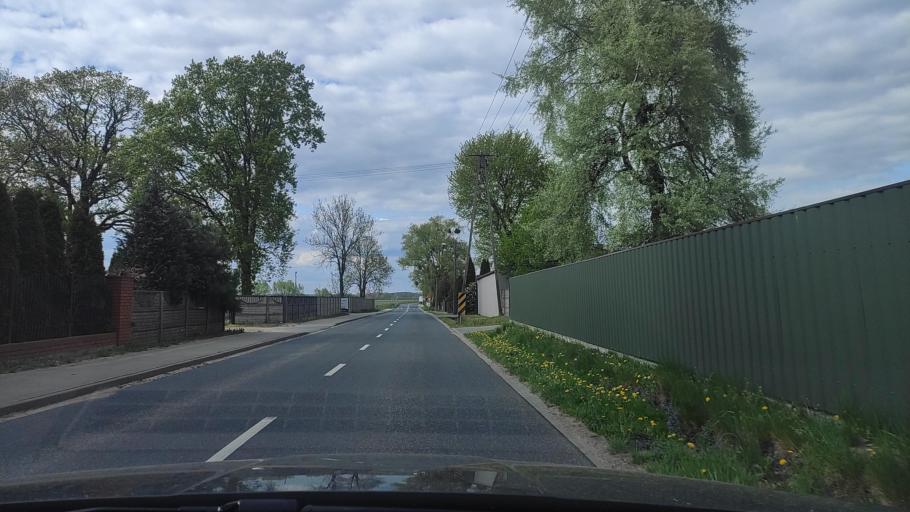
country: PL
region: Greater Poland Voivodeship
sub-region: Powiat poznanski
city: Swarzedz
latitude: 52.4254
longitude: 17.1578
